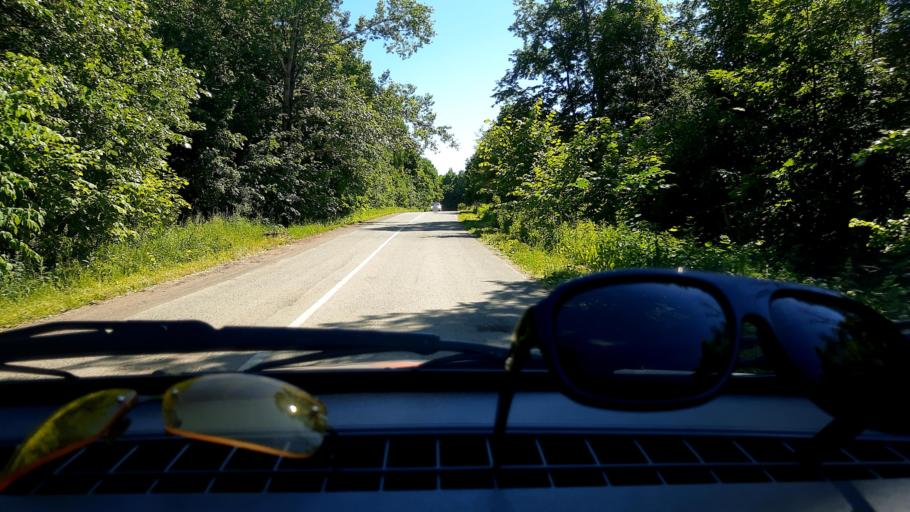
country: RU
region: Bashkortostan
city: Ulu-Telyak
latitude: 54.8100
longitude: 57.0369
